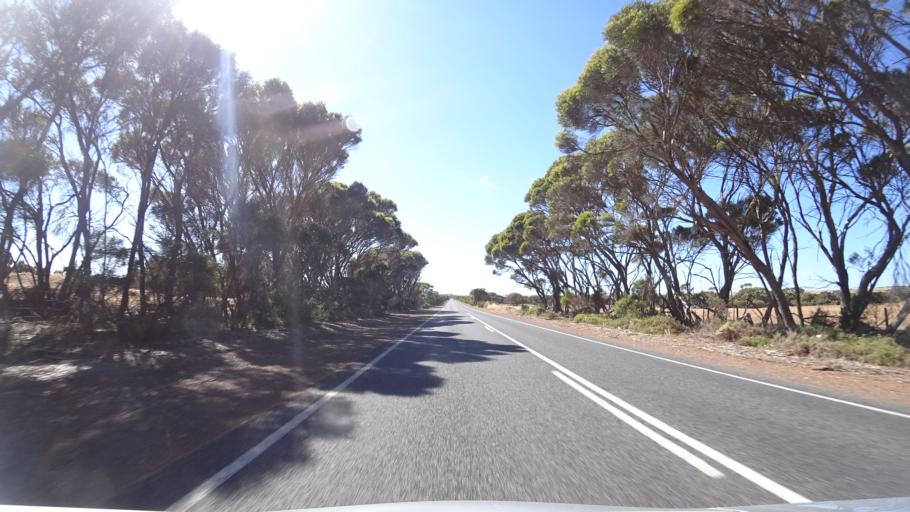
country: AU
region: South Australia
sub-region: Kangaroo Island
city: Kingscote
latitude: -35.7330
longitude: 137.5690
